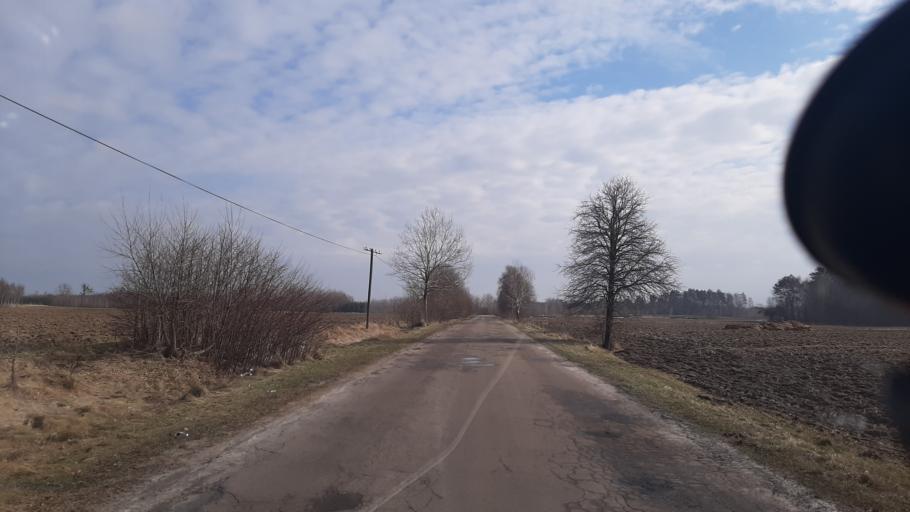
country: PL
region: Lublin Voivodeship
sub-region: Powiat lubartowski
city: Uscimow Stary
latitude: 51.4680
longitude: 22.9871
